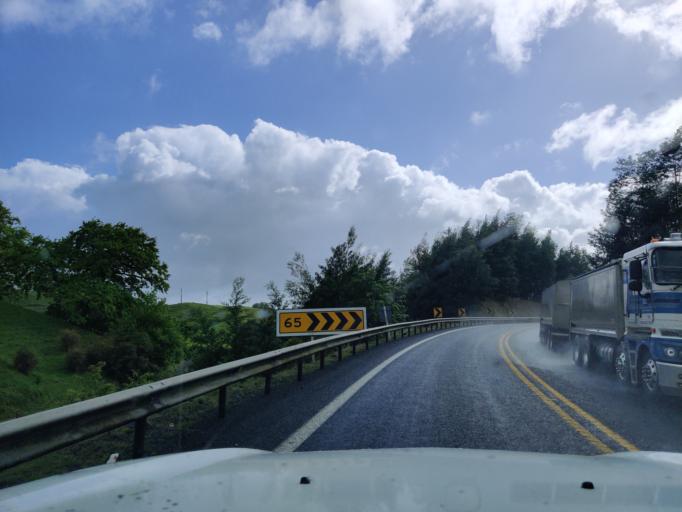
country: NZ
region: Waikato
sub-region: Matamata-Piako District
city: Matamata
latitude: -37.9745
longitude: 175.7433
